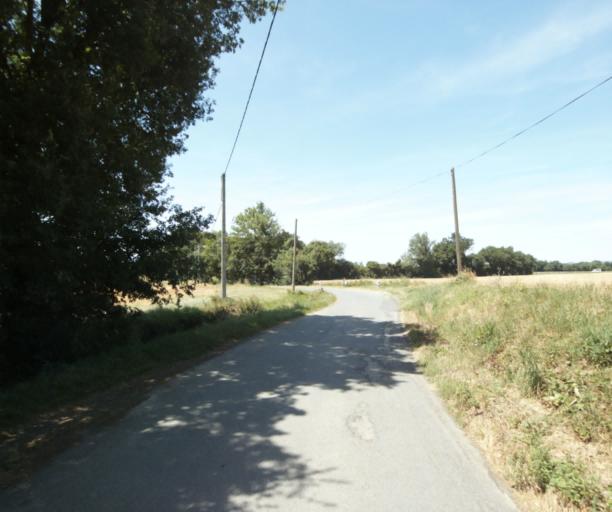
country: FR
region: Midi-Pyrenees
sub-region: Departement du Tarn
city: Soreze
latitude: 43.4907
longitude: 2.0439
